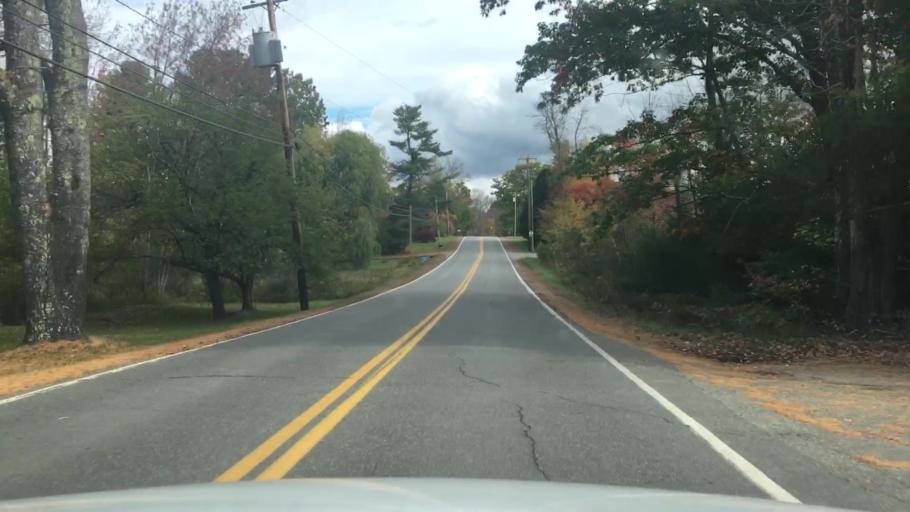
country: US
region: Maine
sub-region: Knox County
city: Hope
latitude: 44.2942
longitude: -69.1127
